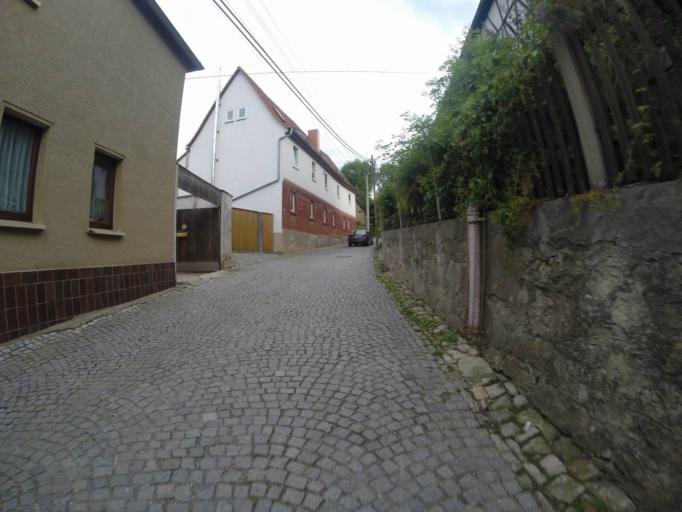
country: DE
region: Thuringia
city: Grosslobichau
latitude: 50.9281
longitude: 11.6517
